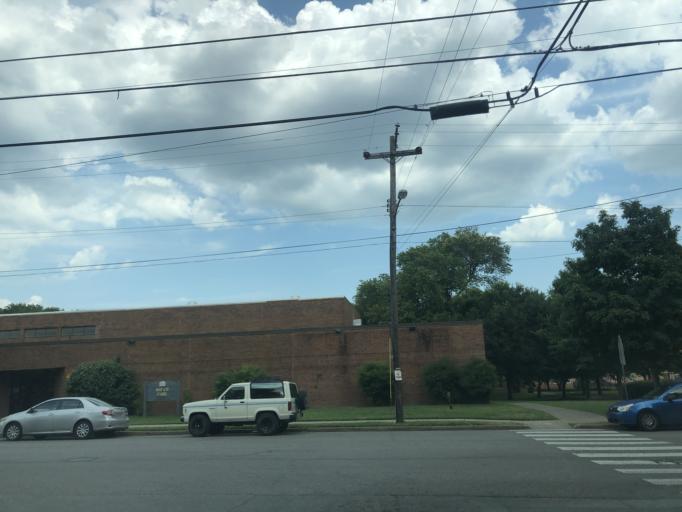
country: US
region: Tennessee
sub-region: Davidson County
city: Nashville
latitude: 36.1505
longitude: -86.7572
